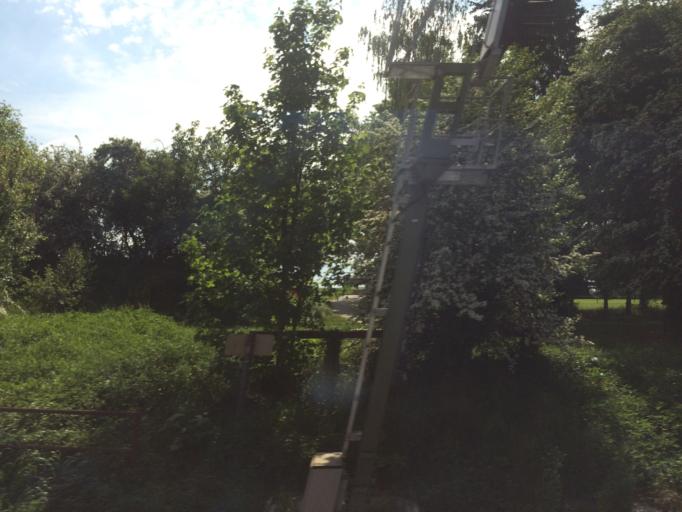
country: DE
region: Bavaria
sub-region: Regierungsbezirk Unterfranken
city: Biebelried
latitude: 49.7950
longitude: 10.0825
